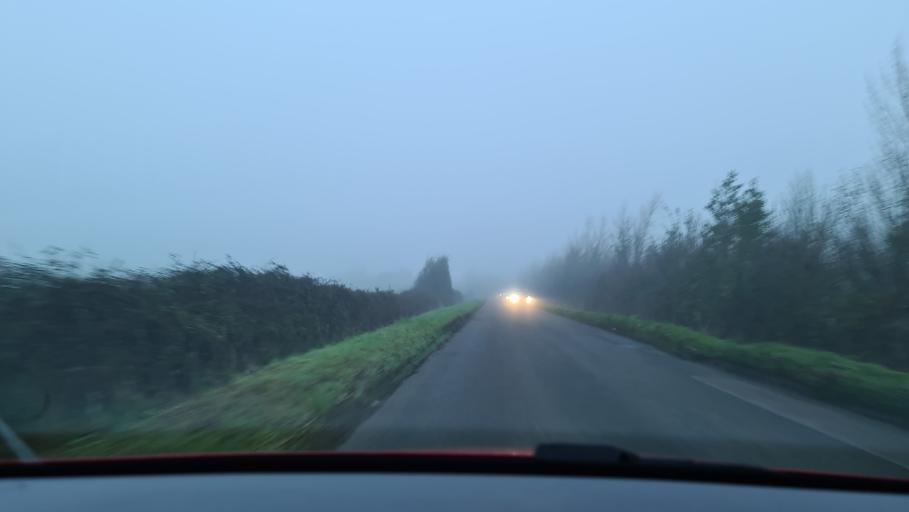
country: GB
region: England
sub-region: Buckinghamshire
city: Waddesdon
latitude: 51.8592
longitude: -0.8753
